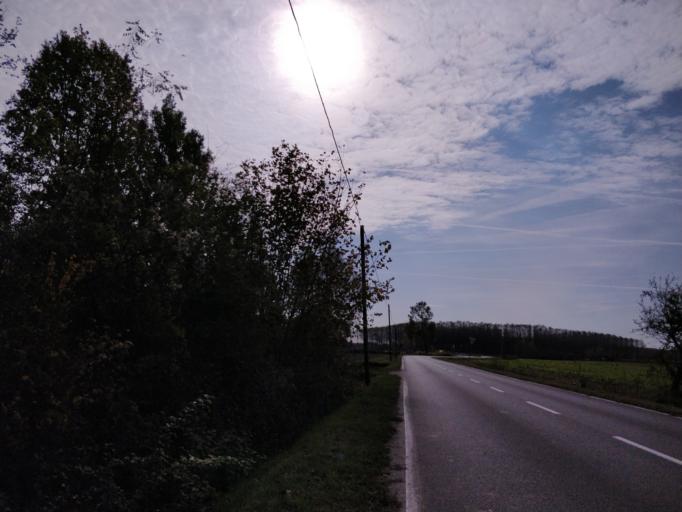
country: IT
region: Friuli Venezia Giulia
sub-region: Provincia di Udine
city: Bertiolo
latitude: 45.9160
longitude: 13.0477
